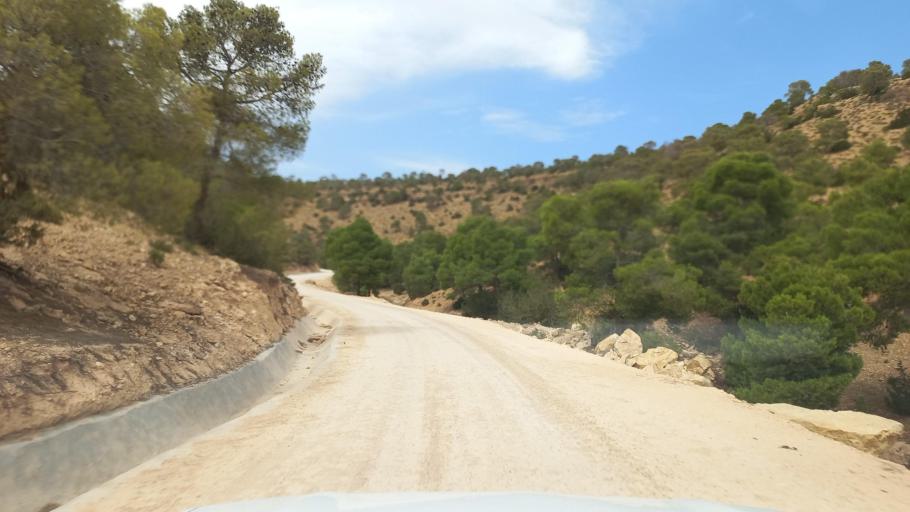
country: TN
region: Al Qasrayn
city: Kasserine
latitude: 35.3747
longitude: 8.8877
